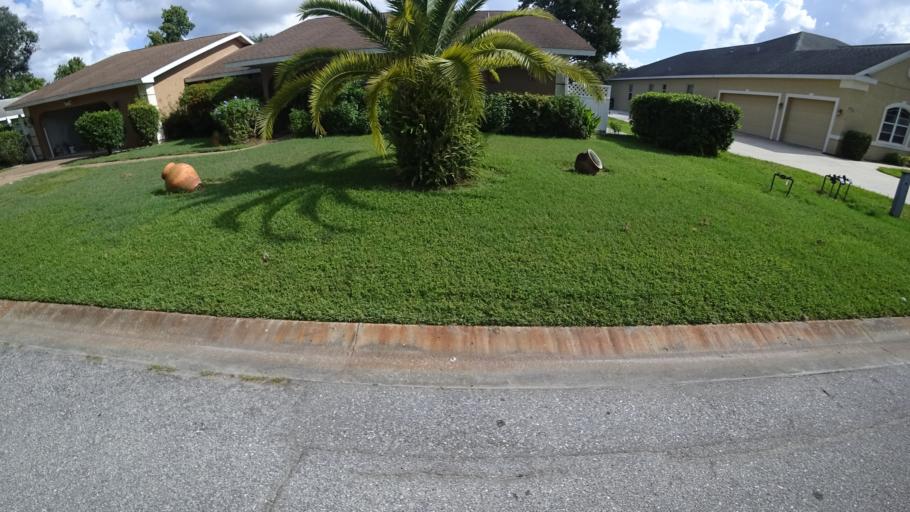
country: US
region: Florida
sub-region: Sarasota County
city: North Sarasota
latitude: 27.4039
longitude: -82.5023
